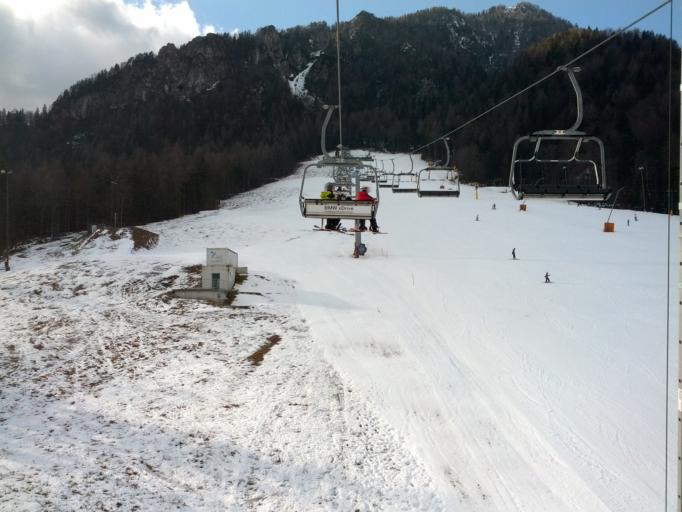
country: SI
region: Kranjska Gora
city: Kranjska Gora
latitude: 46.4825
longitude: 13.7787
